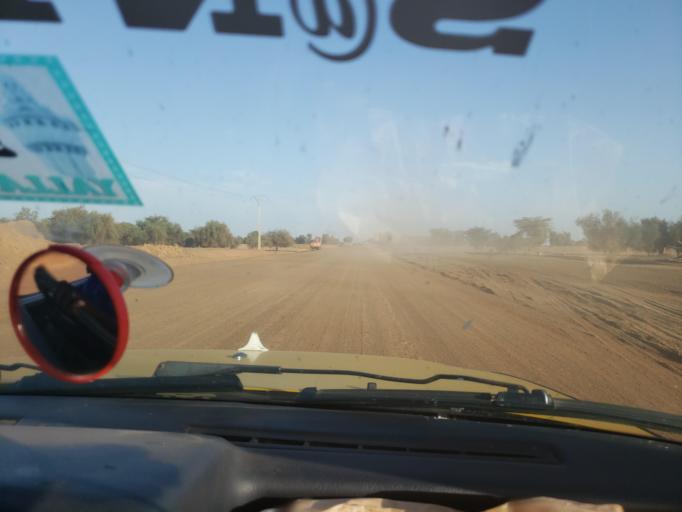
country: SN
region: Louga
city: Dara
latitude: 15.4173
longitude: -15.7157
